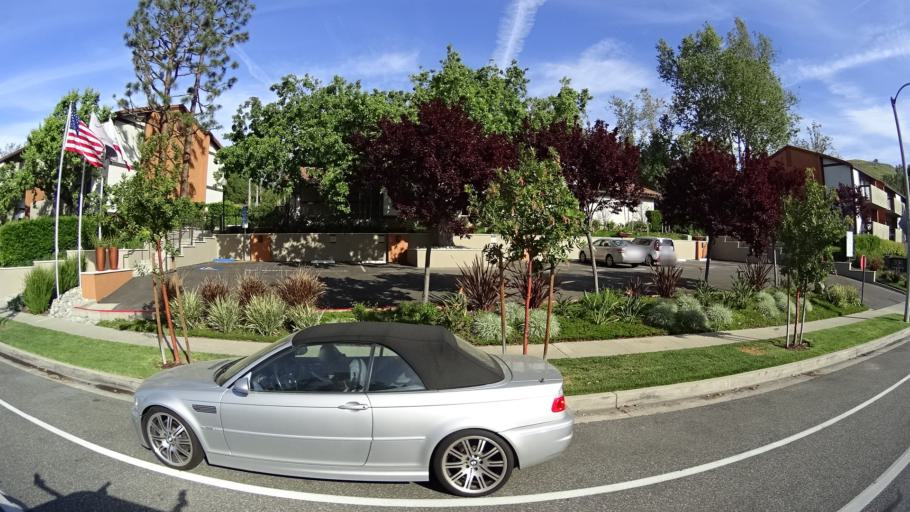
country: US
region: California
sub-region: Ventura County
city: Casa Conejo
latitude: 34.1920
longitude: -118.8891
